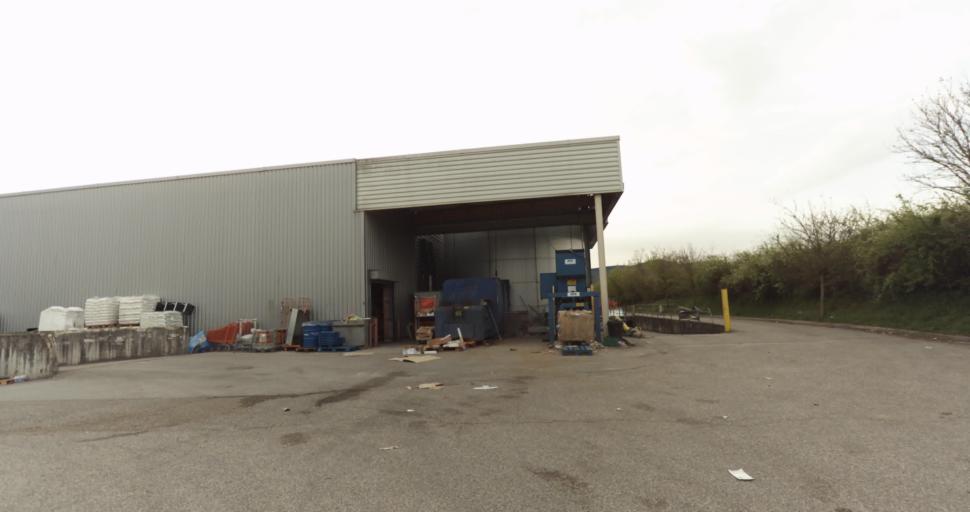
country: FR
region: Rhone-Alpes
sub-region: Departement de l'Ain
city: Amberieu-en-Bugey
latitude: 45.9718
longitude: 5.3365
